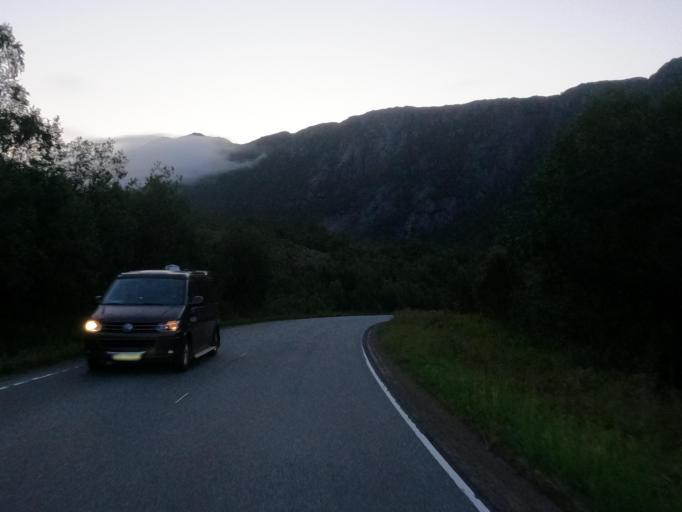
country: NO
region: Nordland
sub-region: Lodingen
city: Lodingen
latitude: 68.5558
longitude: 15.7465
